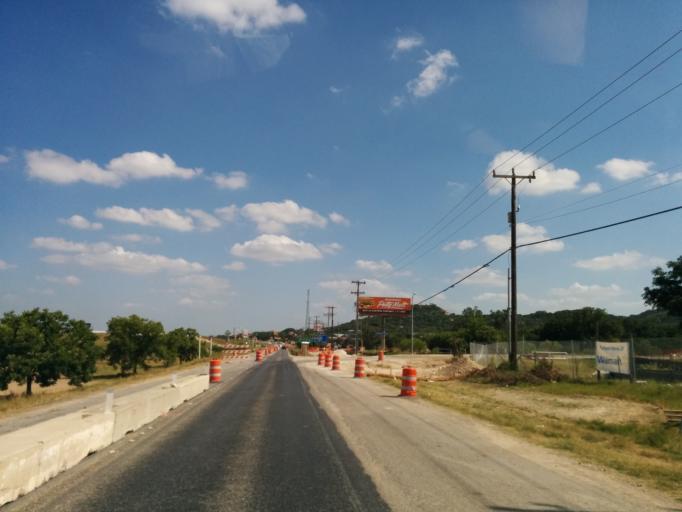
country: US
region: Texas
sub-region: Bexar County
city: Cross Mountain
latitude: 29.6689
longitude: -98.6334
